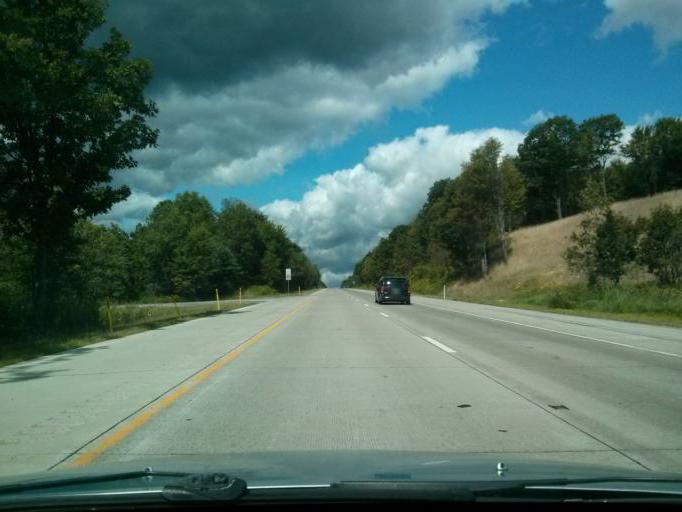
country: US
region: Pennsylvania
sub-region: Jefferson County
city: Falls Creek
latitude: 41.1524
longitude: -78.8049
